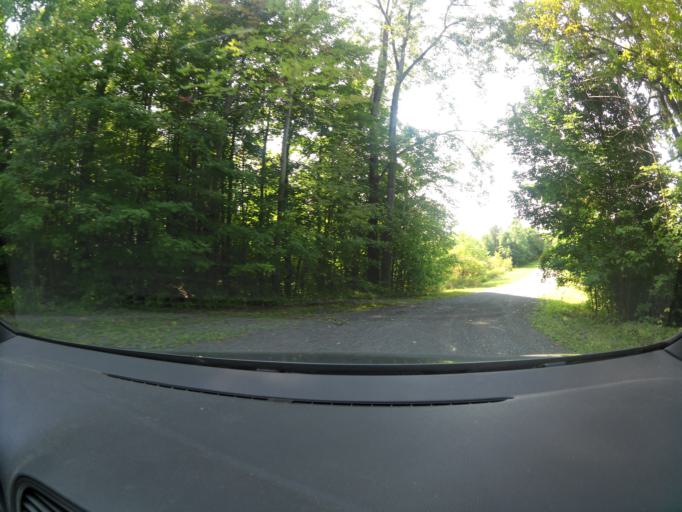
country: CA
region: Ontario
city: Arnprior
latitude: 45.5056
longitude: -76.2022
